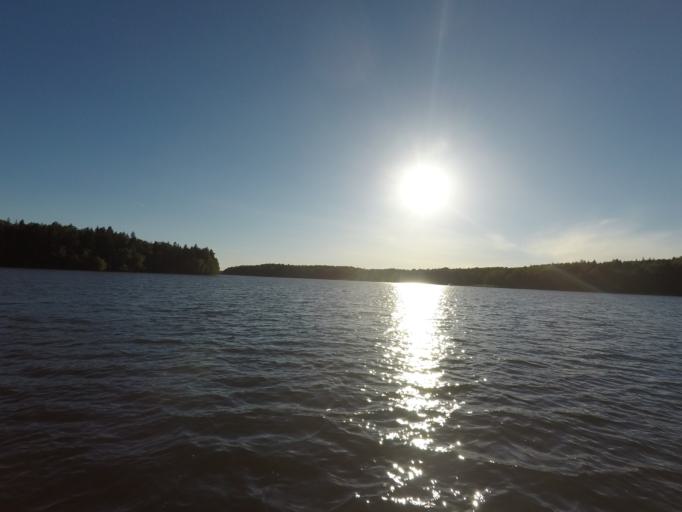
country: SE
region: Soedermanland
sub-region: Eskilstuna Kommun
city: Torshalla
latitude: 59.4704
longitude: 16.4179
